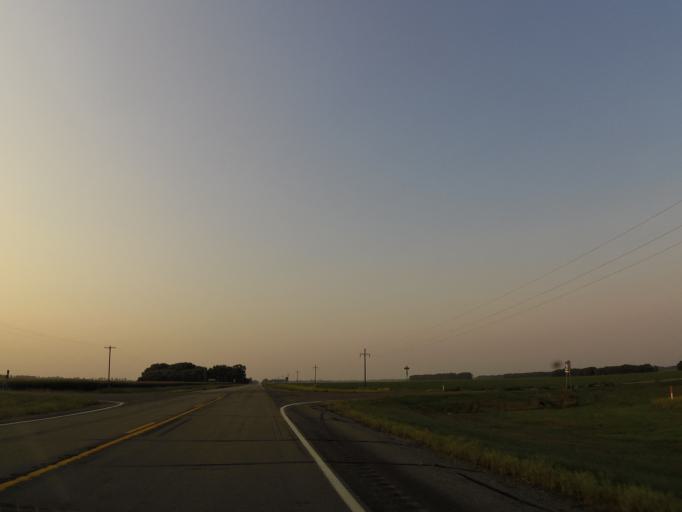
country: US
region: North Dakota
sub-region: Grand Forks County
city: Larimore
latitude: 47.8160
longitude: -97.6234
